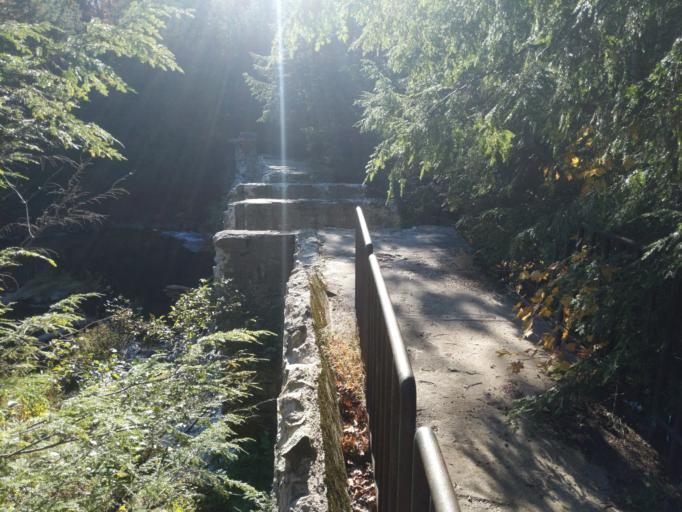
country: CA
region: Quebec
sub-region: Outaouais
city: Wakefield
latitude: 45.5383
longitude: -75.8671
